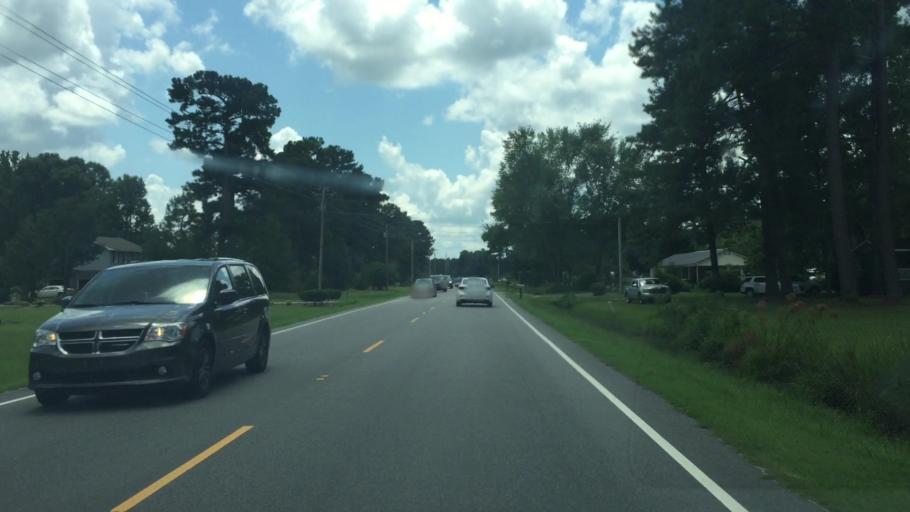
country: US
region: North Carolina
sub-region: Columbus County
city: Chadbourn
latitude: 34.2394
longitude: -78.8225
